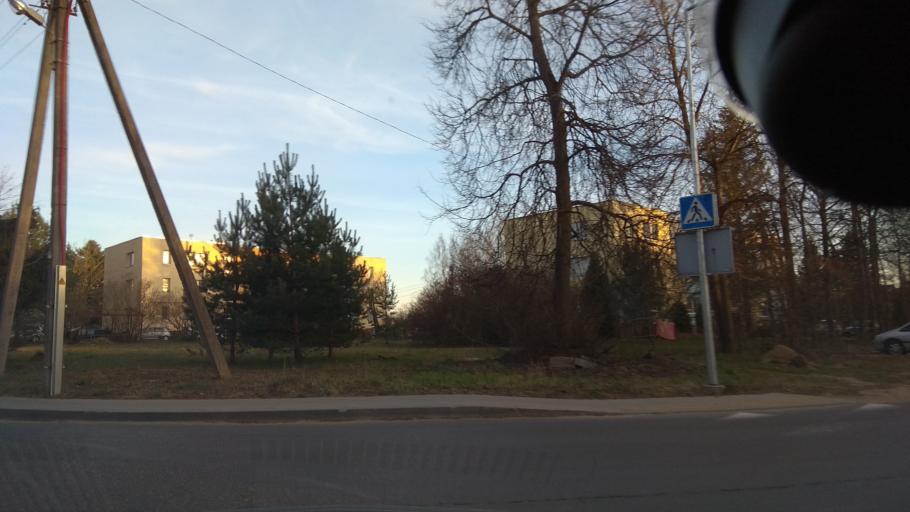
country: LT
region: Vilnius County
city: Pasilaiciai
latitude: 54.7619
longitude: 25.2094
